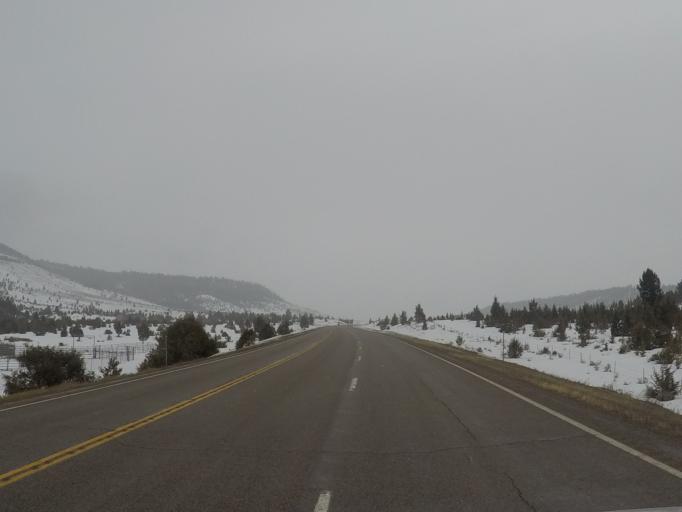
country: US
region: Montana
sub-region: Meagher County
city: White Sulphur Springs
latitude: 46.6668
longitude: -110.8768
